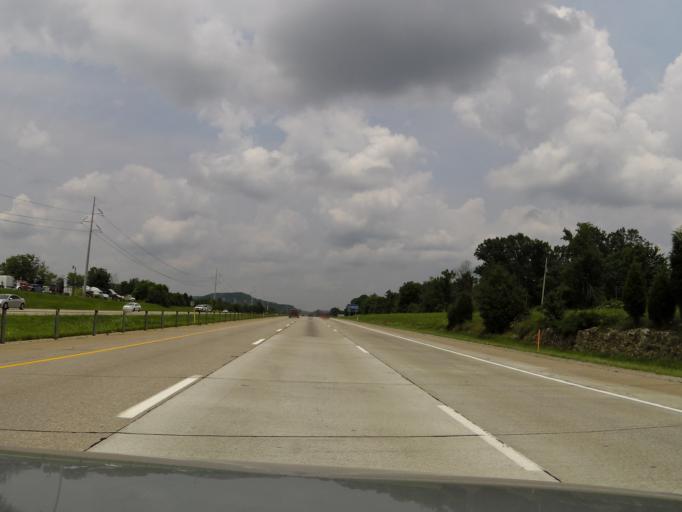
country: US
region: Kentucky
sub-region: Bullitt County
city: Brooks
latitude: 38.0523
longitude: -85.6983
